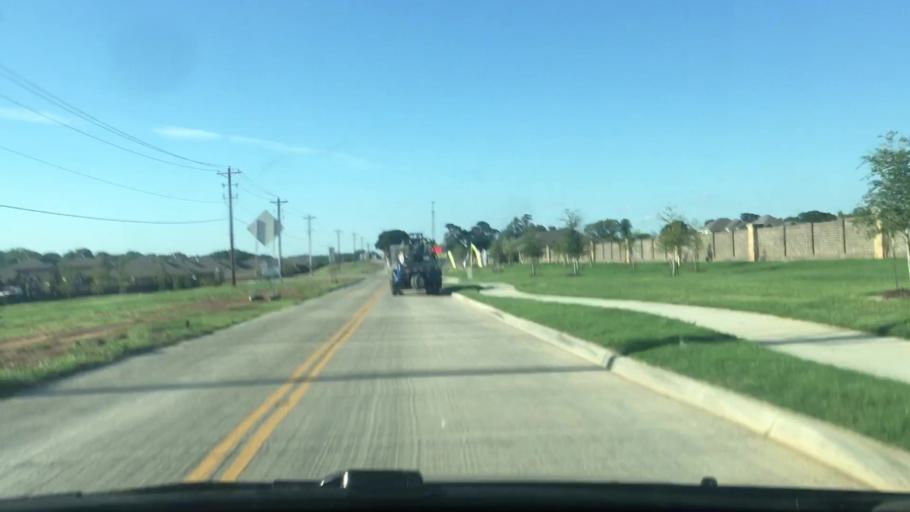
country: US
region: Texas
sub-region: Denton County
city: Cross Roads
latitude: 33.2262
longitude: -96.9762
